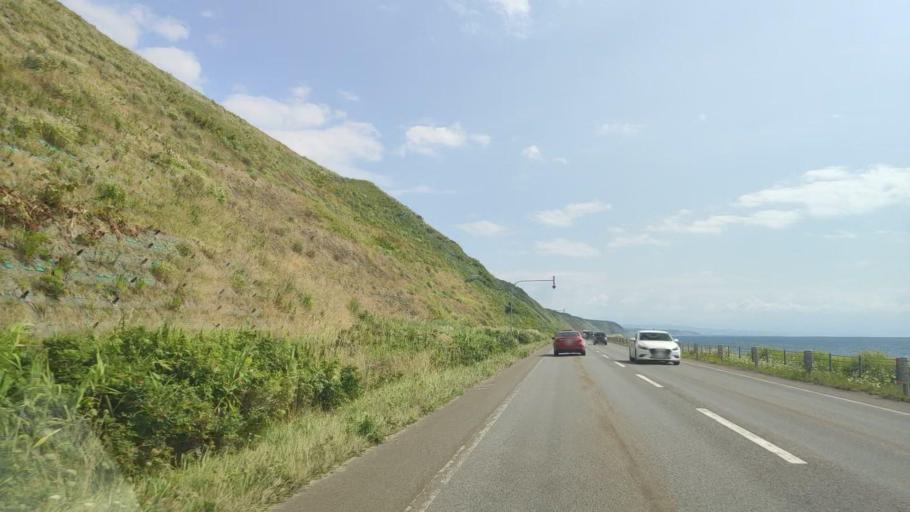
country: JP
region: Hokkaido
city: Rumoi
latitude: 44.0648
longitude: 141.6631
